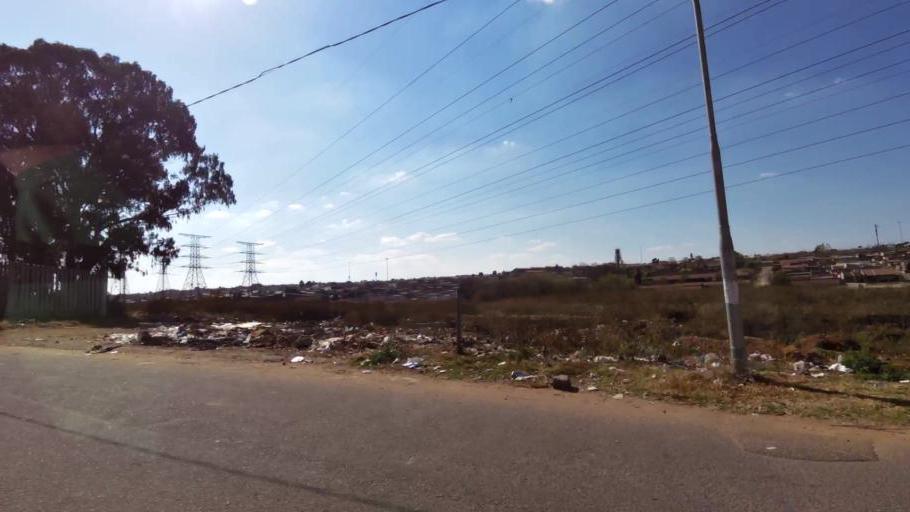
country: ZA
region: Gauteng
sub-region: City of Johannesburg Metropolitan Municipality
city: Soweto
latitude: -26.2337
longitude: 27.8864
